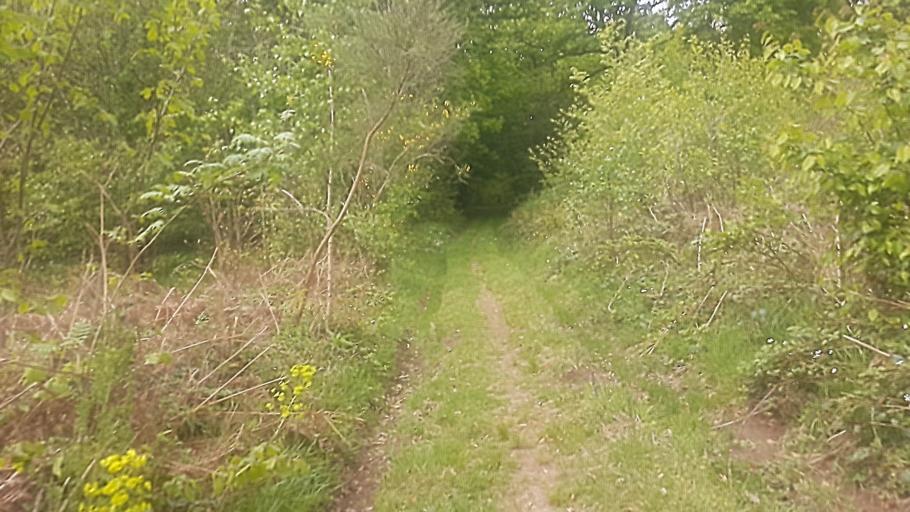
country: FR
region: Champagne-Ardenne
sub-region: Departement des Ardennes
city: Haybes
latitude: 50.0602
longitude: 4.6375
